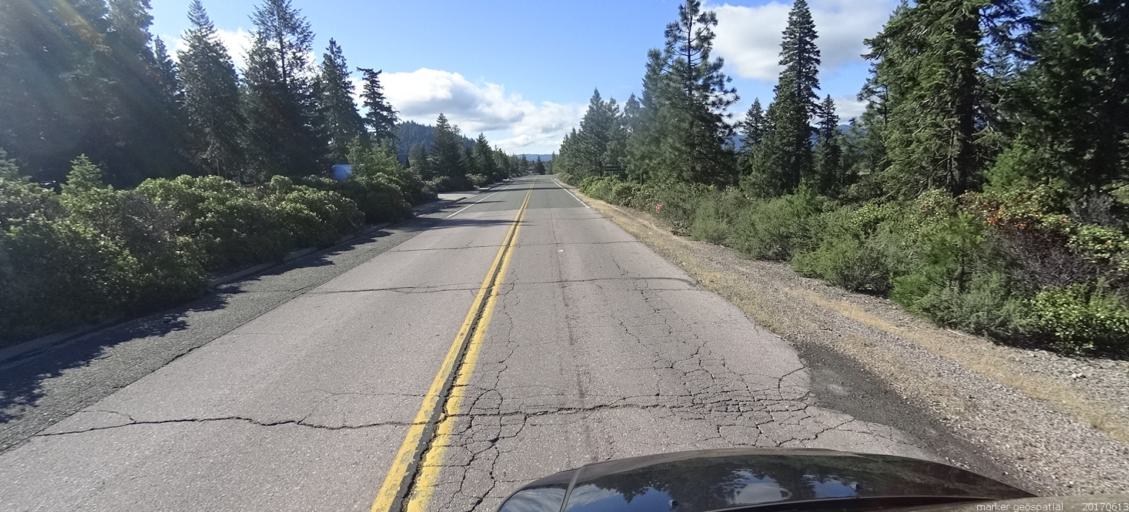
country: US
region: California
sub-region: Siskiyou County
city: Mount Shasta
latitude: 41.3473
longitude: -122.3425
